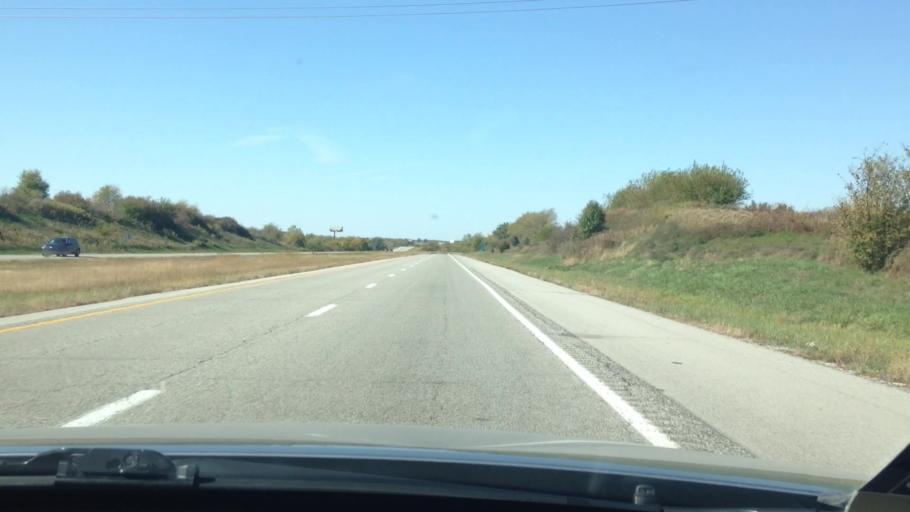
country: US
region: Missouri
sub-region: Platte County
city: Weatherby Lake
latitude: 39.3165
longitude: -94.6829
